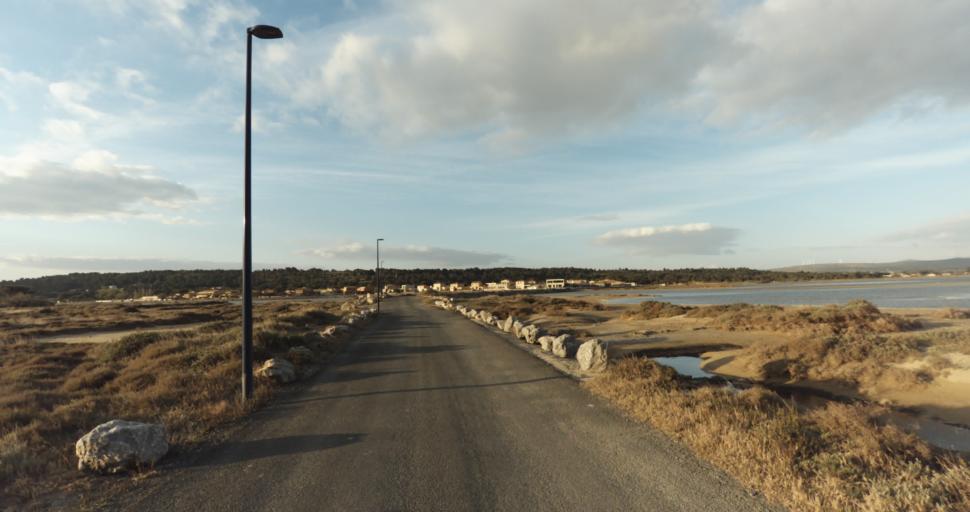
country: FR
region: Languedoc-Roussillon
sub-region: Departement de l'Aude
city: Leucate
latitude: 42.9407
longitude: 3.0278
